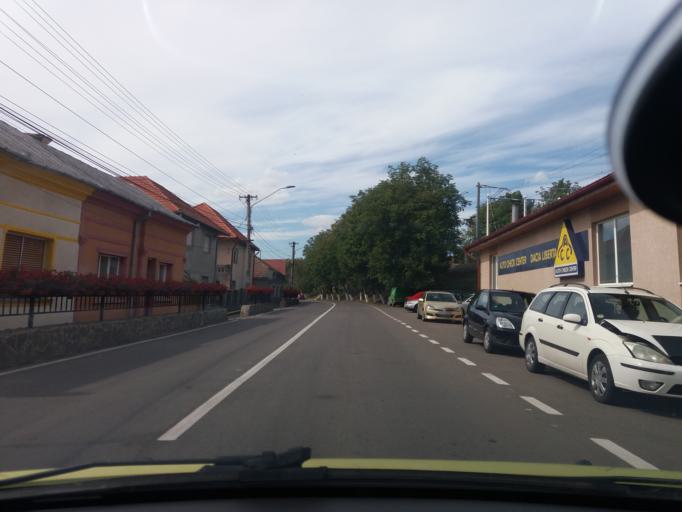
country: RO
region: Alba
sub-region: Municipiul Blaj
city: Veza
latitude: 46.1758
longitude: 23.9329
